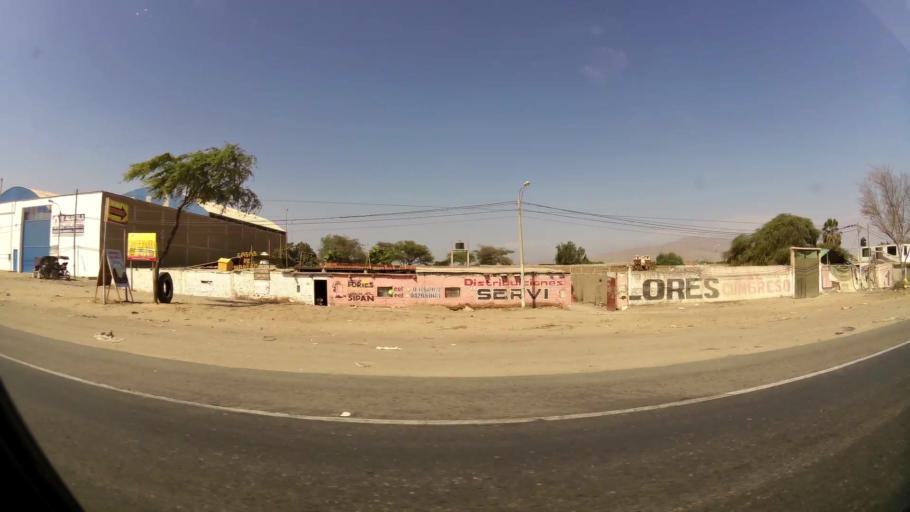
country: PE
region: Lambayeque
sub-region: Provincia de Chiclayo
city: Reque
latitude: -6.8197
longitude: -79.8294
